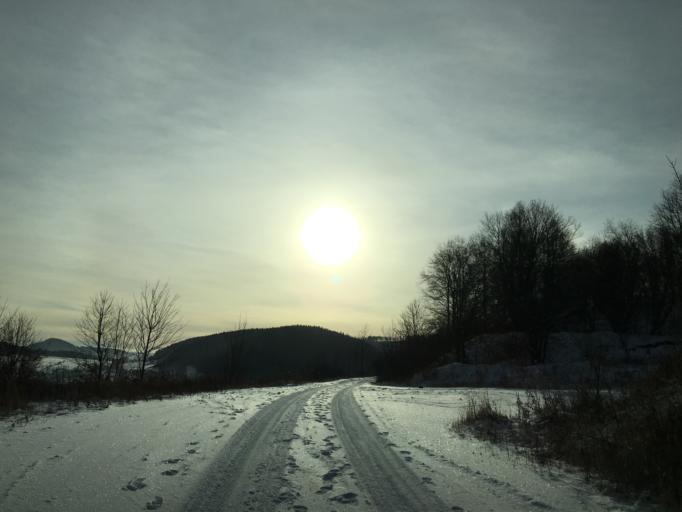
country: PL
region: Lower Silesian Voivodeship
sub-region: Powiat walbrzyski
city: Gluszyca Gorna
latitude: 50.6673
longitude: 16.3561
